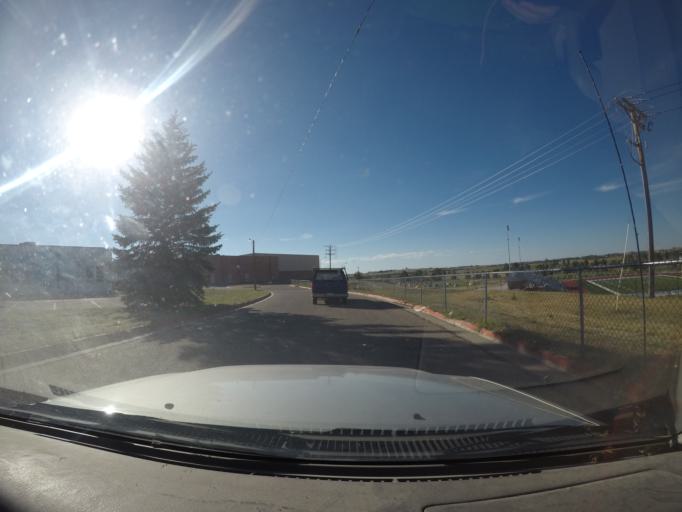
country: US
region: Wyoming
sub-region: Laramie County
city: Fox Farm-College
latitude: 41.1467
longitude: -104.7757
